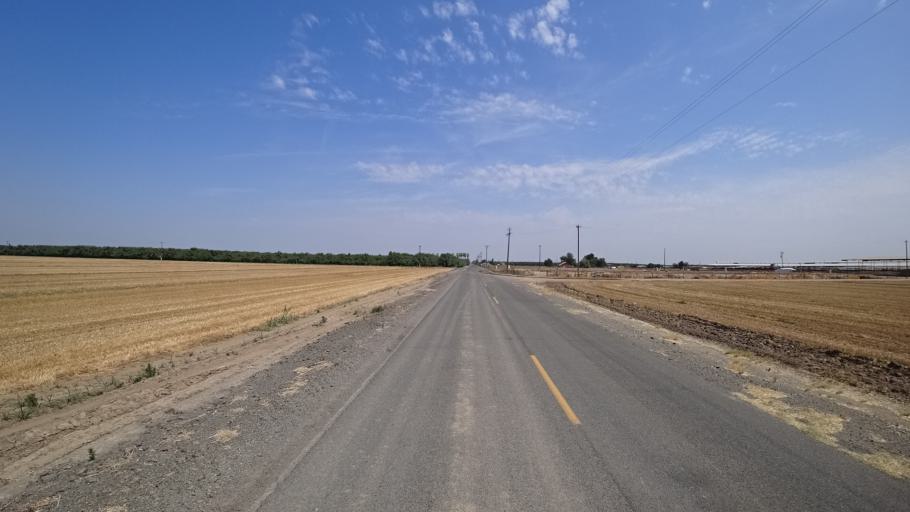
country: US
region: California
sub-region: Kings County
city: Armona
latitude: 36.3375
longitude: -119.7448
